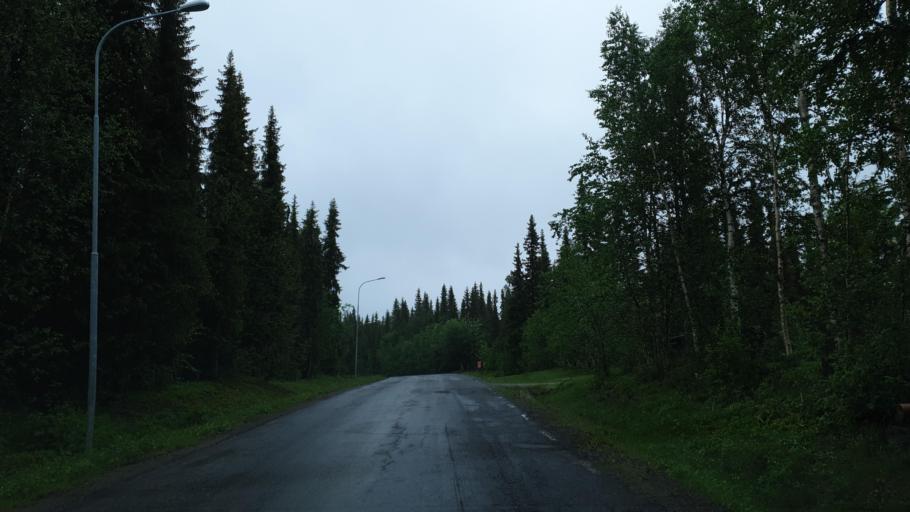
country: SE
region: Vaesterbotten
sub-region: Vilhelmina Kommun
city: Sjoberg
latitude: 65.2389
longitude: 15.9927
